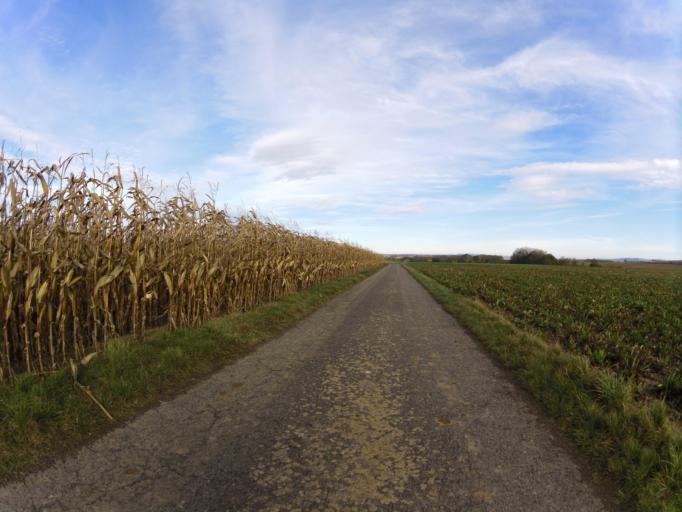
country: DE
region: Bavaria
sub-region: Regierungsbezirk Unterfranken
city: Gaukonigshofen
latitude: 49.6643
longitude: 9.9813
